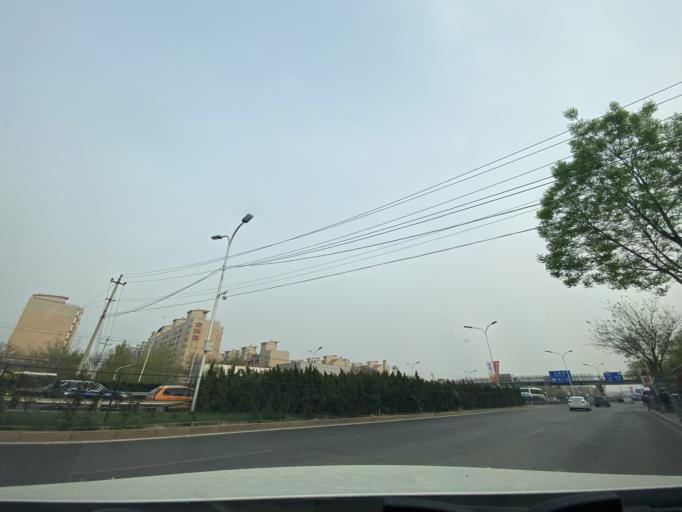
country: CN
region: Beijing
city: Sijiqing
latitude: 39.9417
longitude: 116.2677
